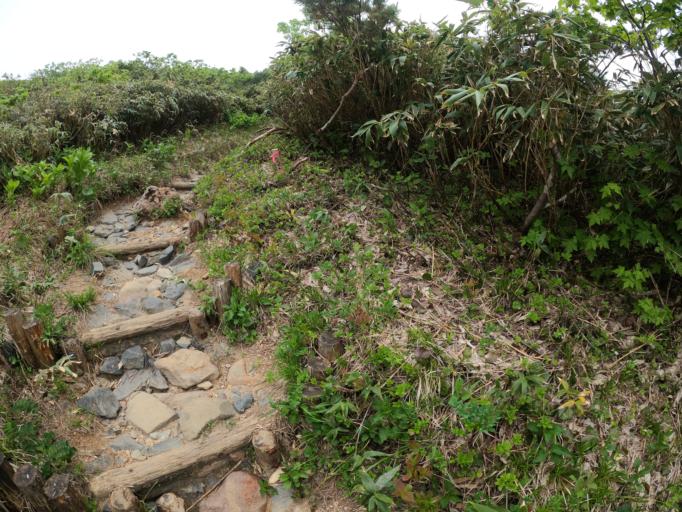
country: JP
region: Iwate
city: Ichinoseki
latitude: 38.9675
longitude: 140.7921
